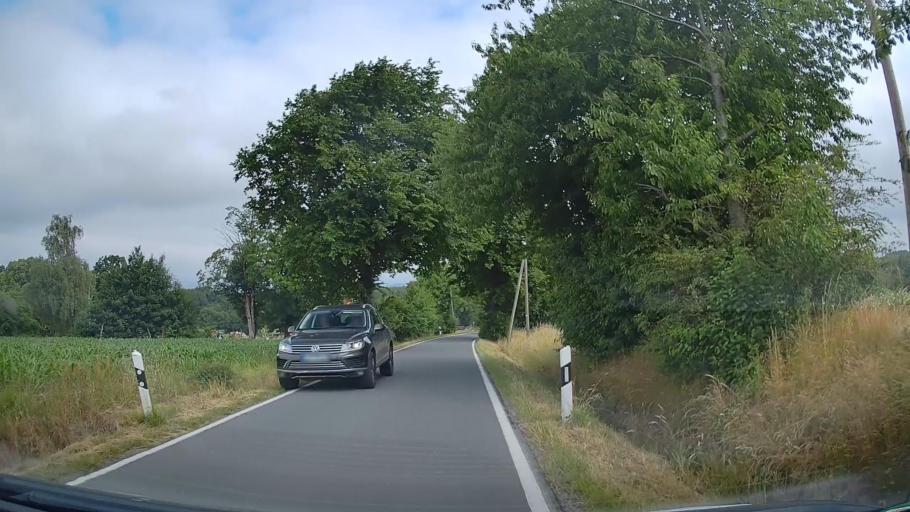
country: DE
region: North Rhine-Westphalia
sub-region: Regierungsbezirk Detmold
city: Barntrup
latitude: 52.0865
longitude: 9.1329
